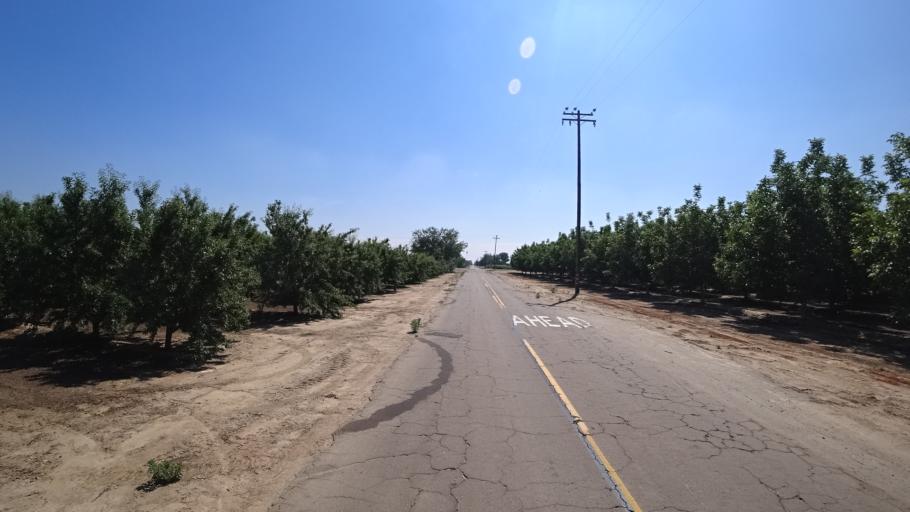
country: US
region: California
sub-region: Fresno County
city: Kingsburg
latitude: 36.4741
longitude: -119.5656
